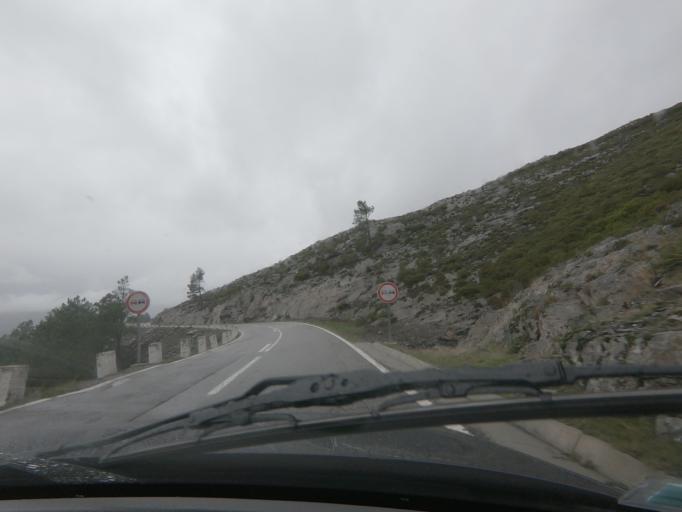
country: PT
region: Vila Real
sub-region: Mondim de Basto
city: Mondim de Basto
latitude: 41.3326
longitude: -7.8765
